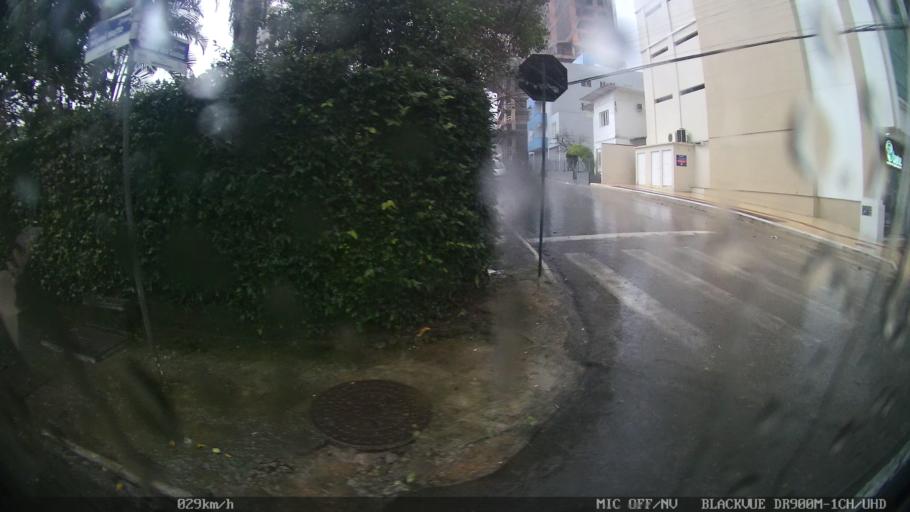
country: BR
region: Santa Catarina
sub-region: Balneario Camboriu
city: Balneario Camboriu
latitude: -26.9695
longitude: -48.6373
